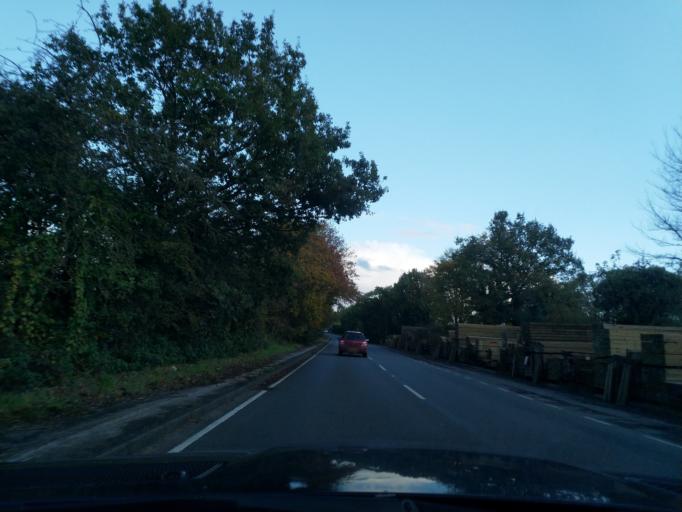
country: GB
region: England
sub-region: Solihull
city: Knowle
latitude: 52.3414
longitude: -1.7564
